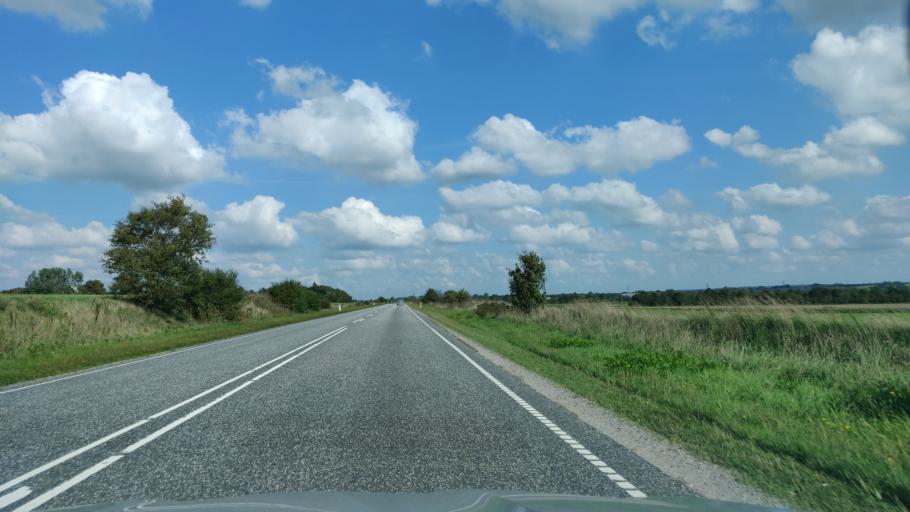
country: DK
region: North Denmark
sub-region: Vesthimmerland Kommune
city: Aars
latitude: 56.7818
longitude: 9.5863
